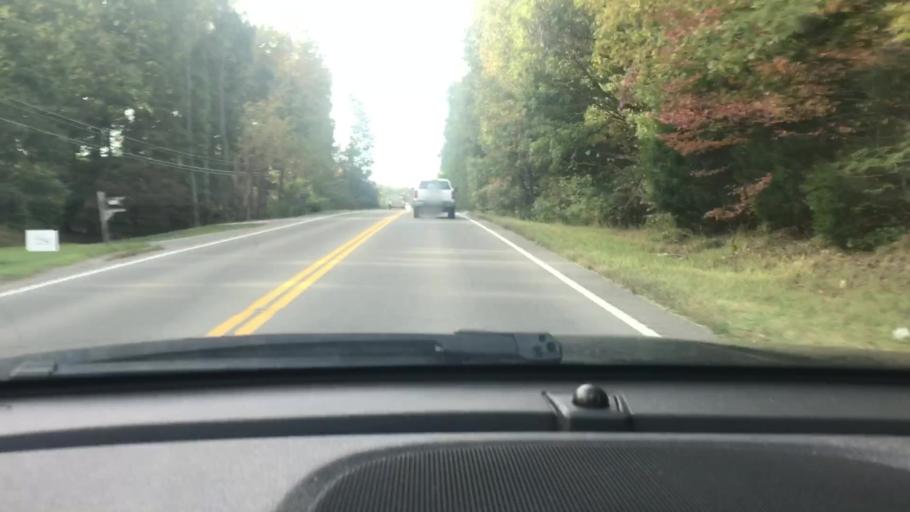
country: US
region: Tennessee
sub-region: Williamson County
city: Fairview
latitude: 35.9872
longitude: -87.1193
